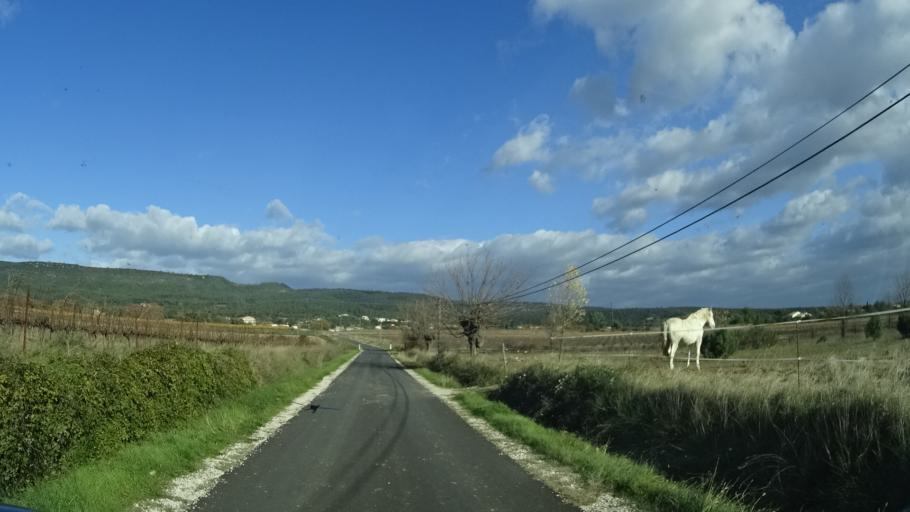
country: FR
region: Languedoc-Roussillon
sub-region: Departement de l'Herault
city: Claret
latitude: 43.8536
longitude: 3.8956
